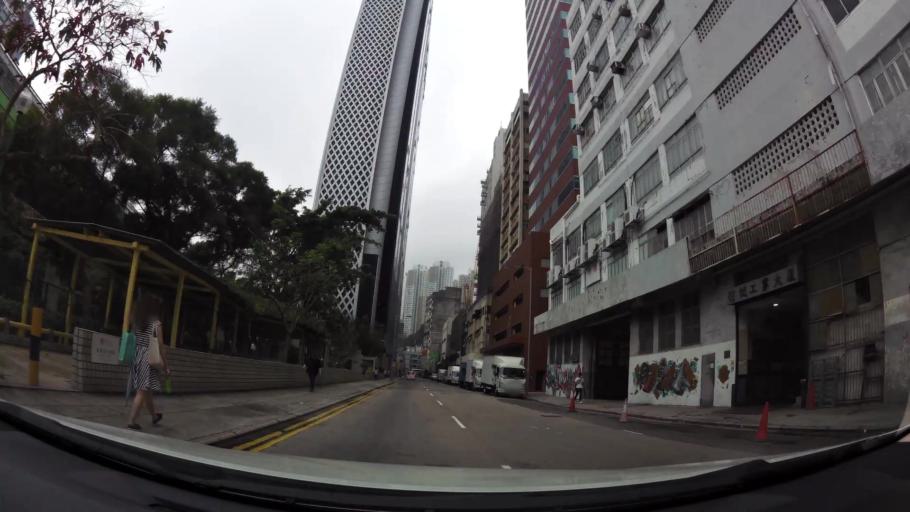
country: HK
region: Wanchai
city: Wan Chai
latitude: 22.2477
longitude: 114.1641
